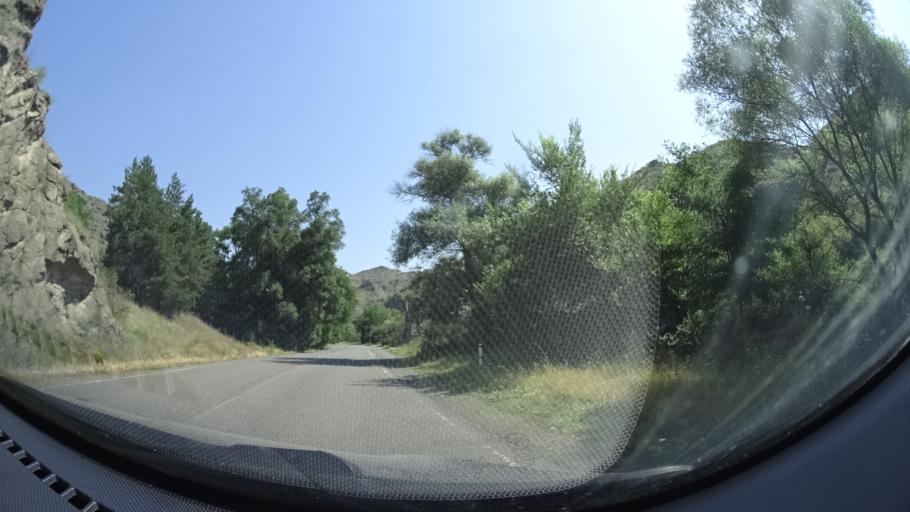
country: GE
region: Samtskhe-Javakheti
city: Akhaltsikhe
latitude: 41.6124
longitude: 43.0992
